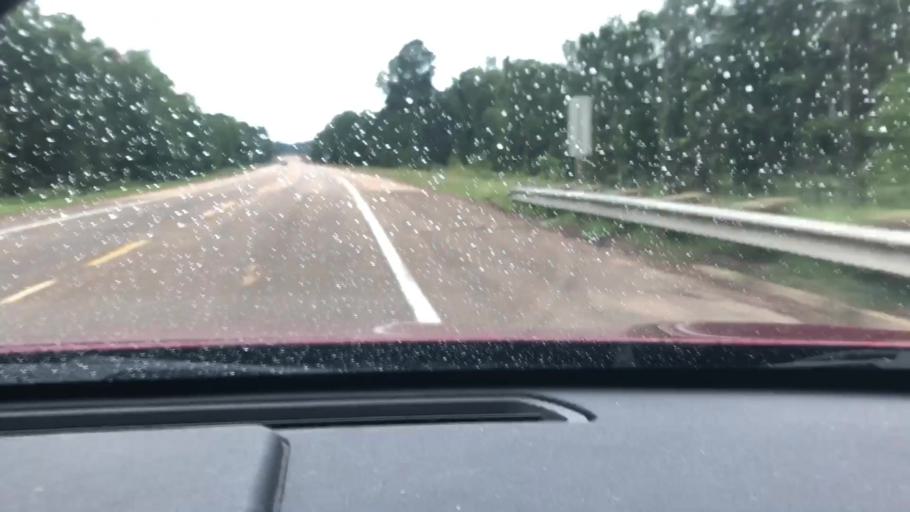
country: US
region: Arkansas
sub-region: Lafayette County
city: Stamps
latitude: 33.3590
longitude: -93.4147
